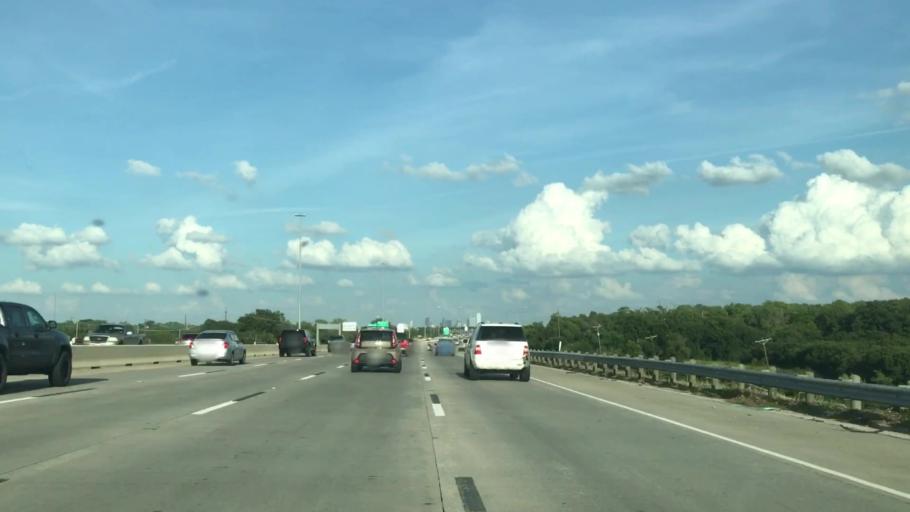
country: US
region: Texas
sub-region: Dallas County
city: Irving
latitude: 32.7643
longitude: -96.9350
